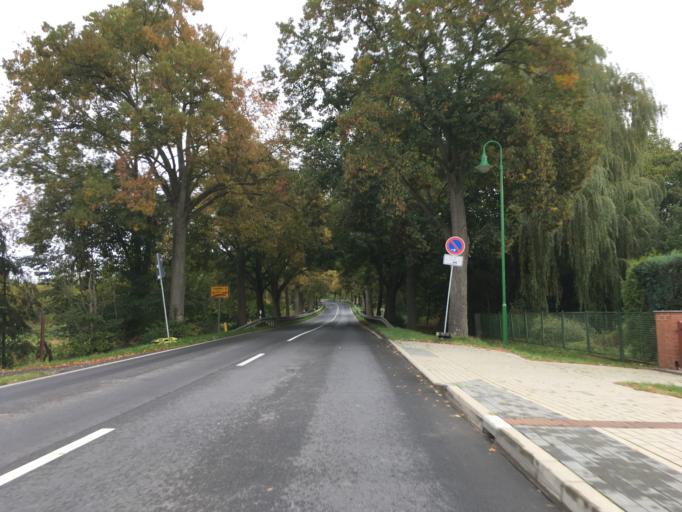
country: DE
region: Brandenburg
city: Werftpfuhl
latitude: 52.6840
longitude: 13.8434
